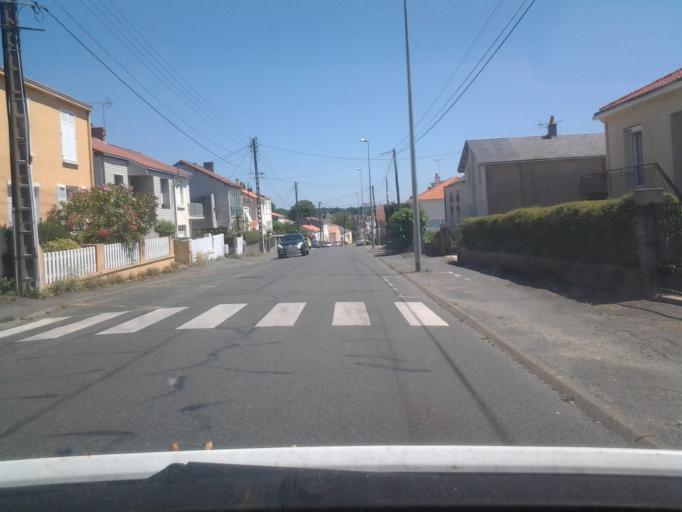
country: FR
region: Pays de la Loire
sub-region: Departement de la Vendee
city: La Roche-sur-Yon
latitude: 46.6636
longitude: -1.4073
